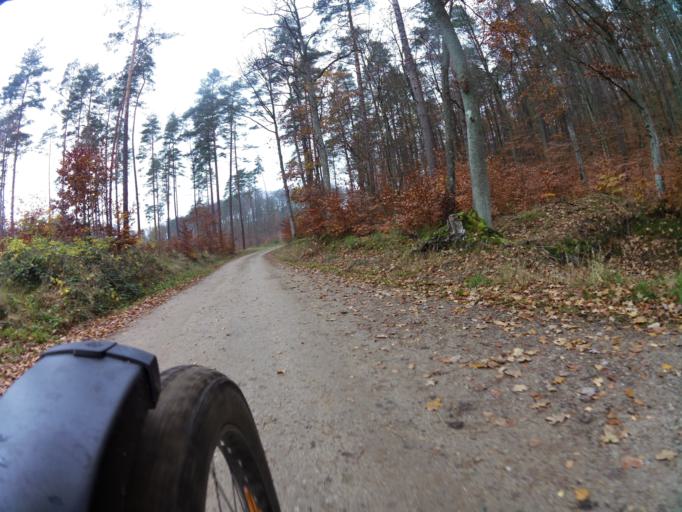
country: PL
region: Pomeranian Voivodeship
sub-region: Powiat wejherowski
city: Orle
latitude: 54.7025
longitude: 18.1464
